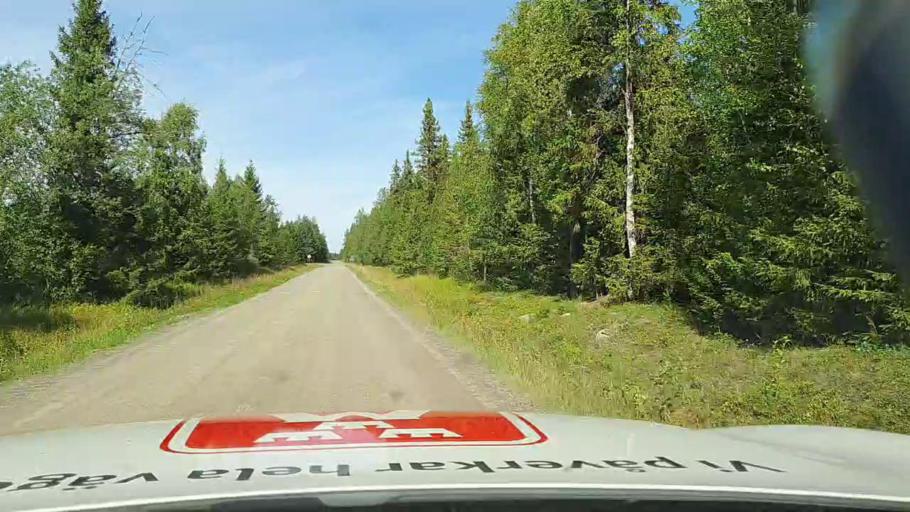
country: SE
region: Jaemtland
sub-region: Stroemsunds Kommun
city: Stroemsund
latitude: 63.7399
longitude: 15.2400
